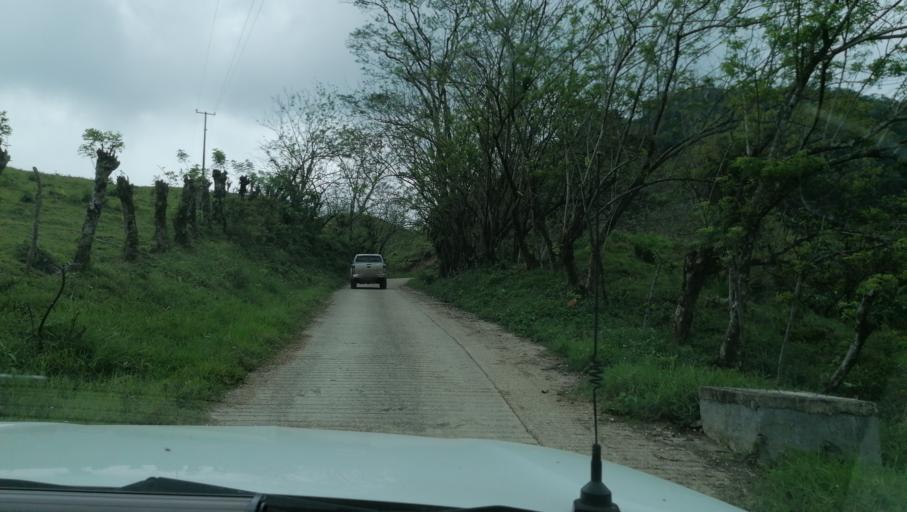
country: MX
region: Chiapas
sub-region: Ocotepec
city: San Pablo Huacano
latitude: 17.2690
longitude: -93.2486
